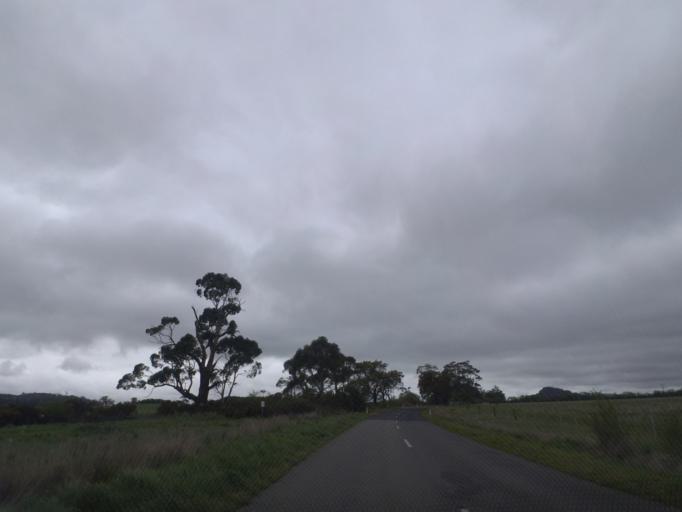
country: AU
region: Victoria
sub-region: Hume
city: Sunbury
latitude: -37.3240
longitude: 144.5617
